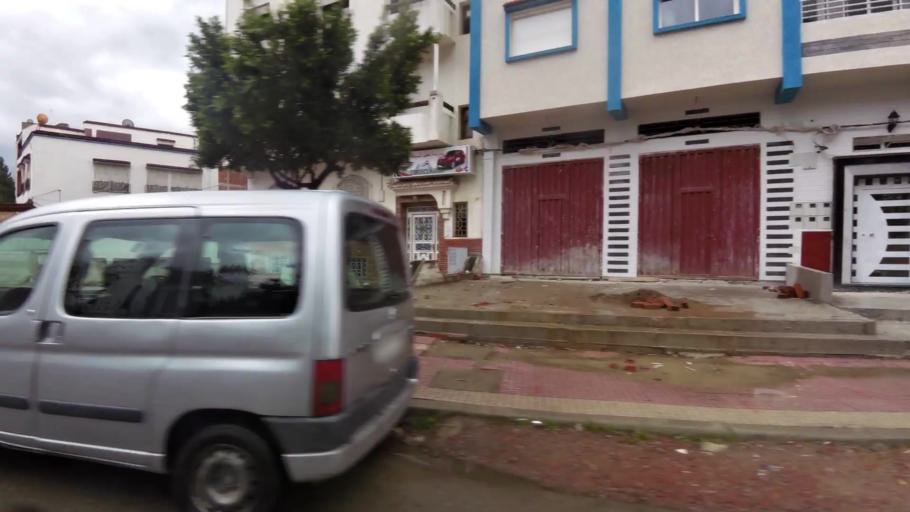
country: MA
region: Tanger-Tetouan
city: Chefchaouene
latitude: 35.1694
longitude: -5.2723
